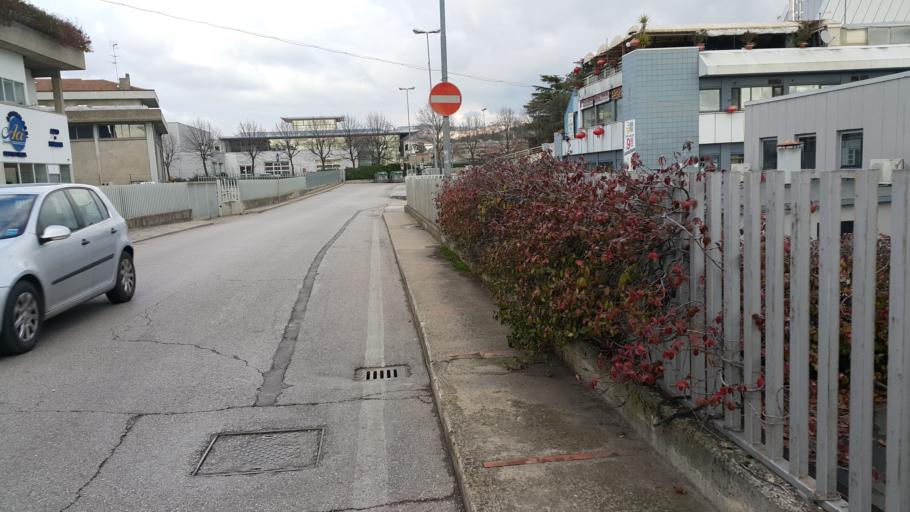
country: IT
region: Umbria
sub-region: Provincia di Perugia
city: Perugia
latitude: 43.0873
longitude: 12.3668
